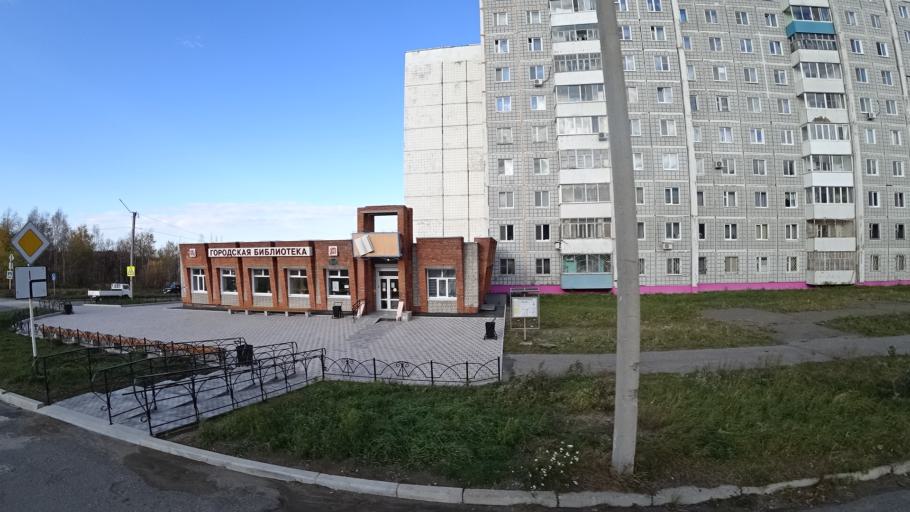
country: RU
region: Khabarovsk Krai
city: Amursk
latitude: 50.2430
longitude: 136.9203
